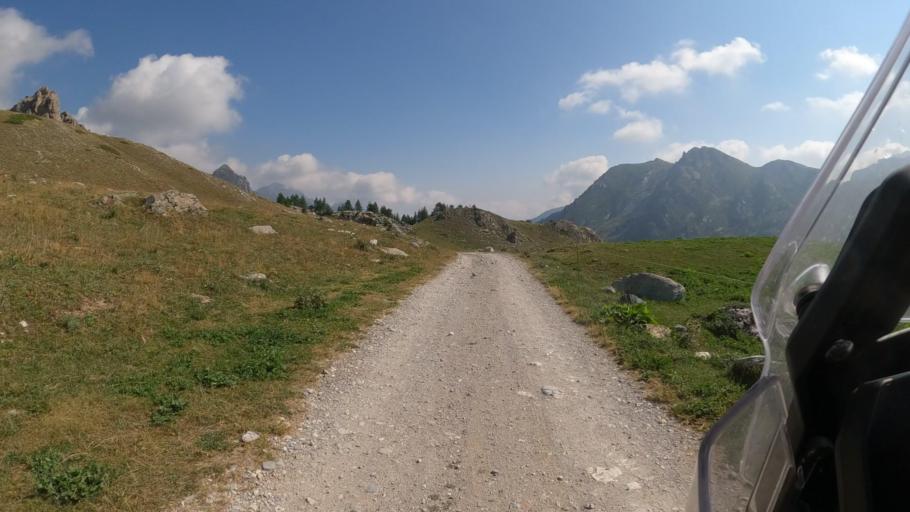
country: IT
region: Piedmont
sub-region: Provincia di Cuneo
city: Pietraporzio
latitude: 44.4025
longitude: 7.0377
